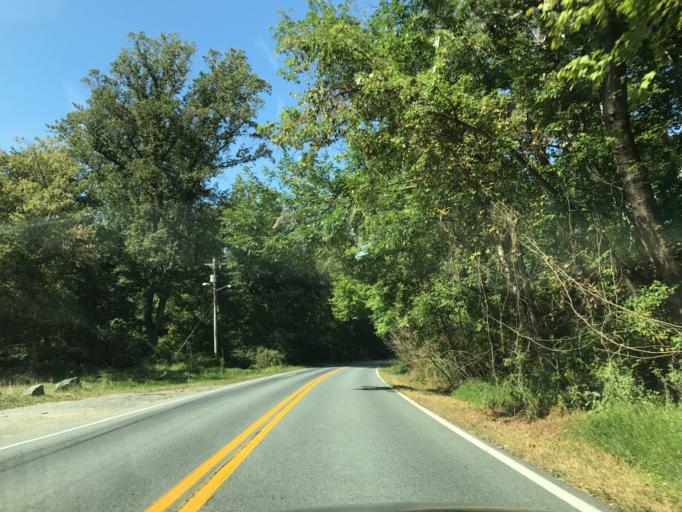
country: US
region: Maryland
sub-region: Harford County
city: Havre de Grace
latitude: 39.6342
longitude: -76.1477
